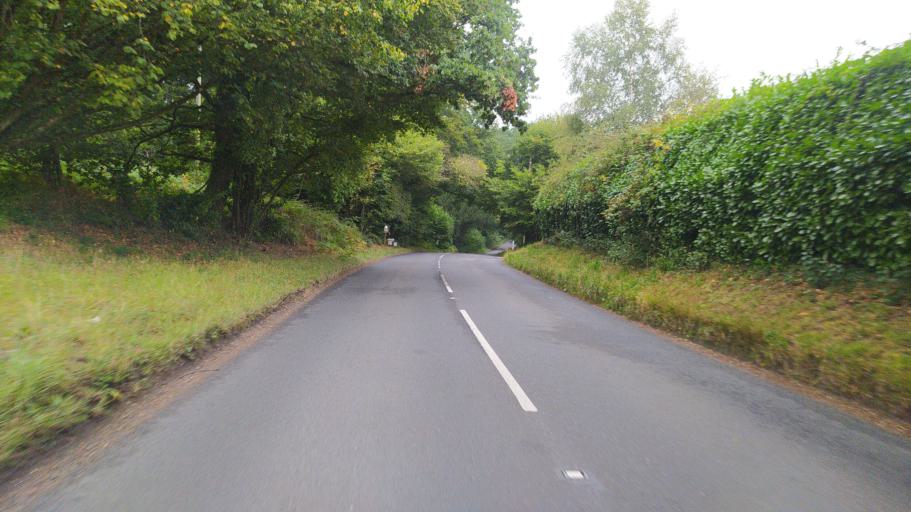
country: GB
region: England
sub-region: Dorset
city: Verwood
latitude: 50.8858
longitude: -1.9076
